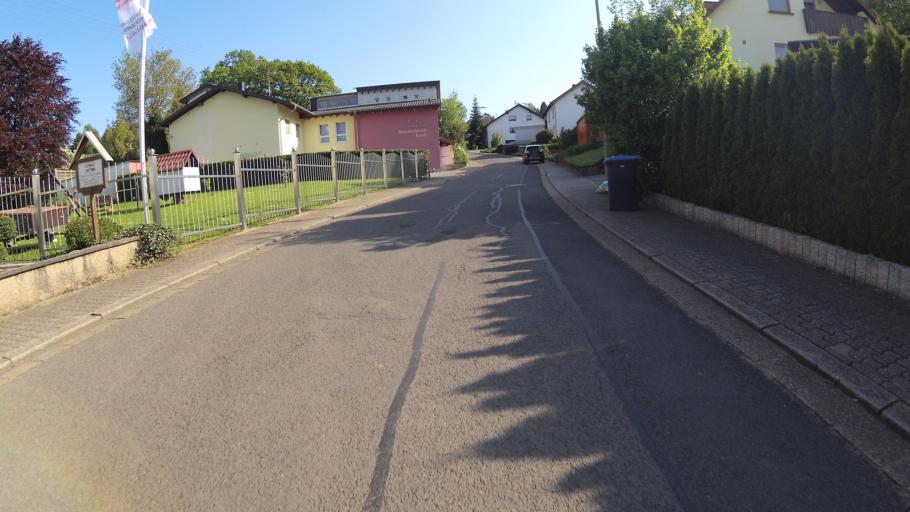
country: DE
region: Saarland
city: Illingen
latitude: 49.3980
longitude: 7.0290
